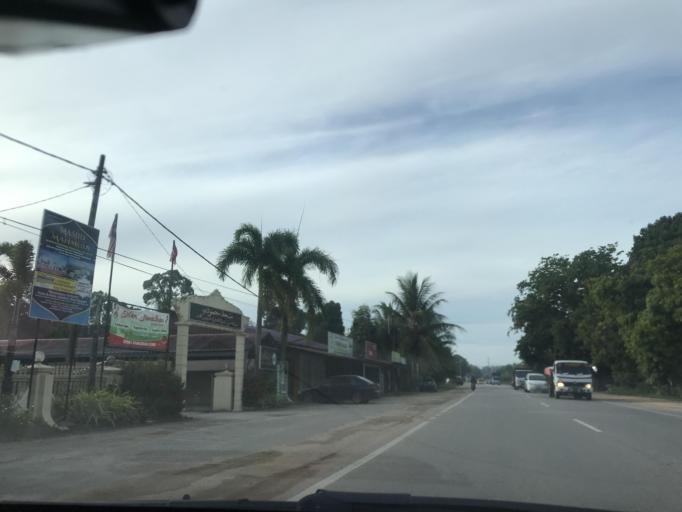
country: MY
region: Kelantan
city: Kampung Lemal
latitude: 5.9993
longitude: 102.1854
